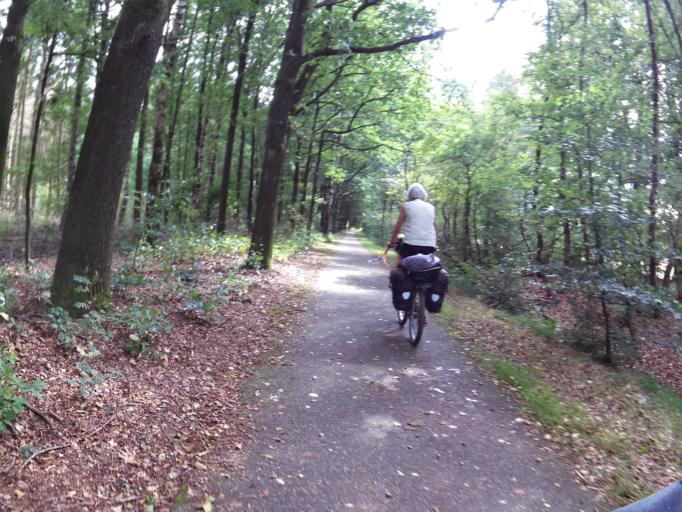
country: NL
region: Drenthe
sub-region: Gemeente Borger-Odoorn
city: Borger
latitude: 52.9442
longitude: 6.7497
